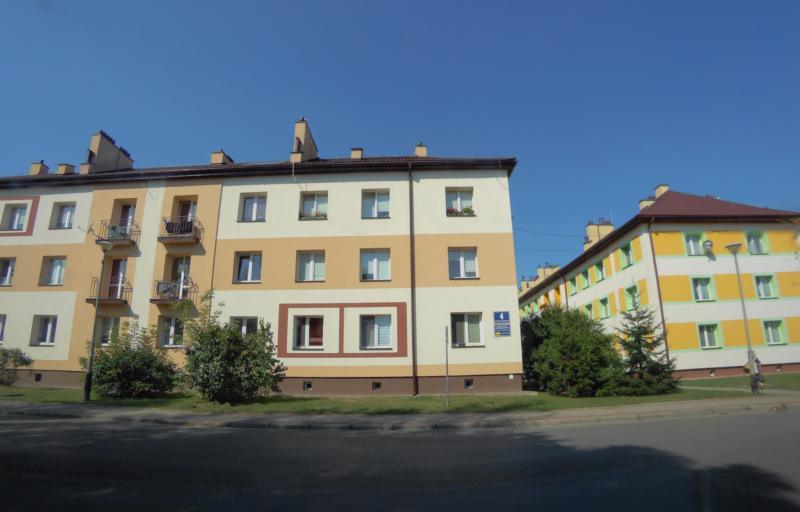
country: PL
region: Subcarpathian Voivodeship
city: Nowa Sarzyna
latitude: 50.3196
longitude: 22.3467
